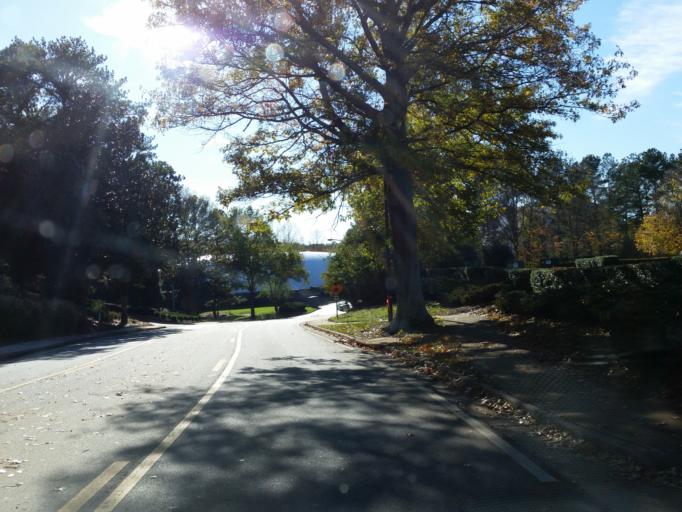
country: US
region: Georgia
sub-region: Cobb County
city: Vinings
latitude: 33.9039
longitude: -84.4648
